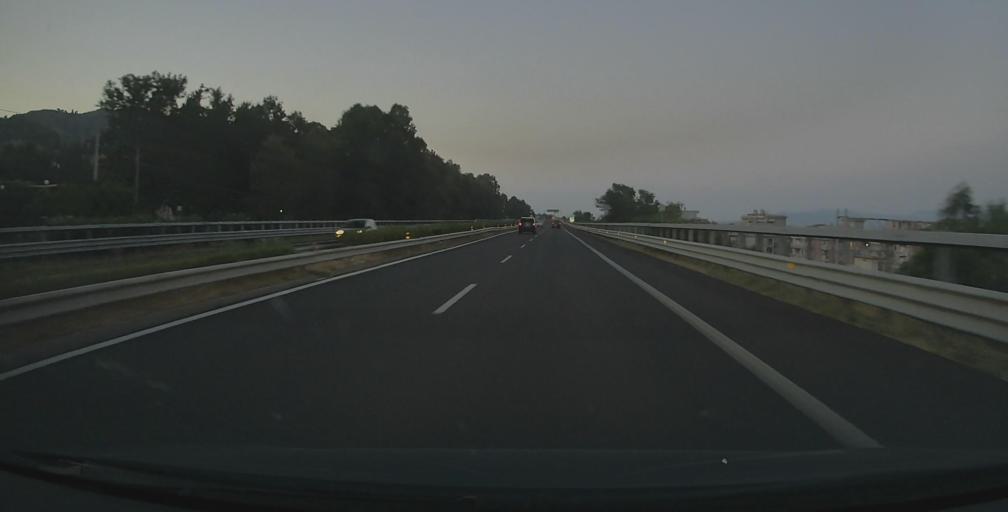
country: IT
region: Sicily
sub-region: Messina
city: Larderia
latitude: 38.1126
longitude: 15.5094
